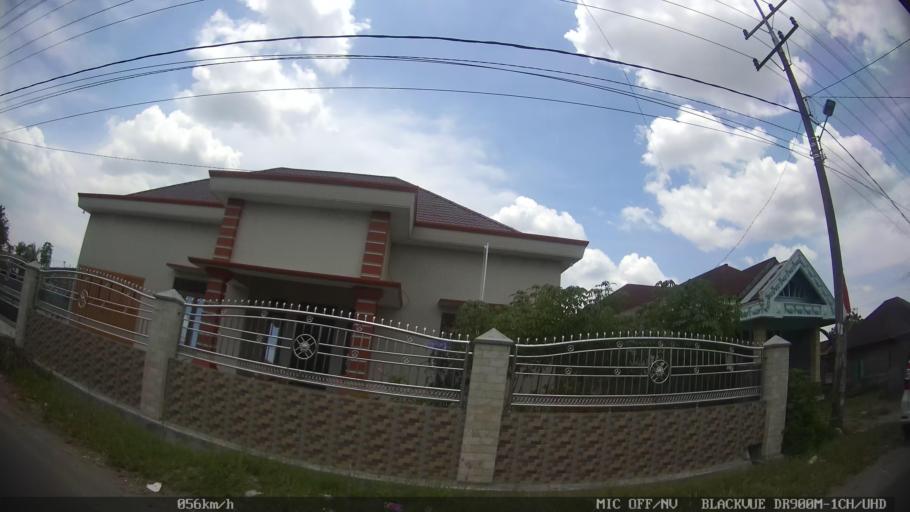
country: ID
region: North Sumatra
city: Binjai
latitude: 3.6279
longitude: 98.5142
